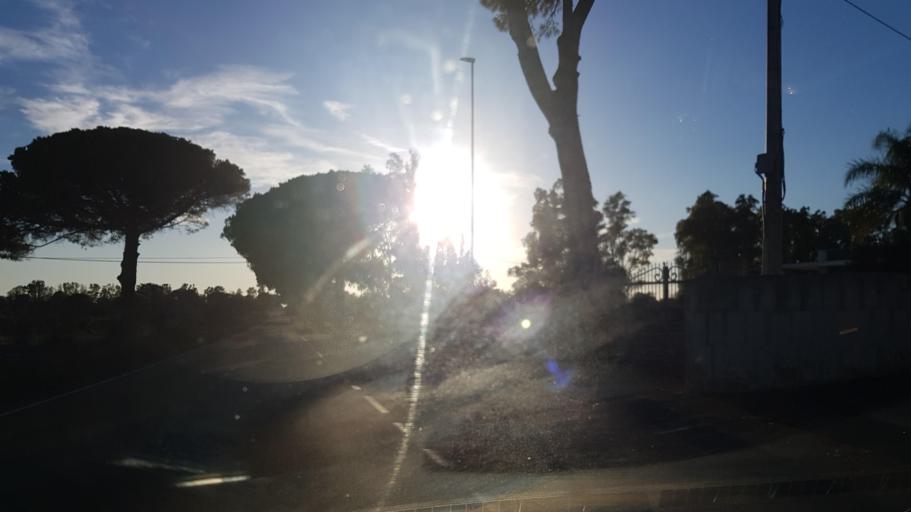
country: IT
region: Apulia
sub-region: Provincia di Lecce
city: Merine
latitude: 40.4219
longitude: 18.2304
